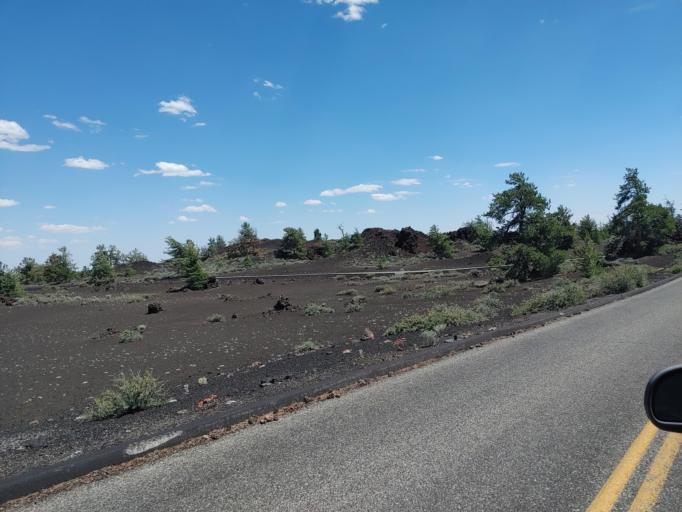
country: US
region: Idaho
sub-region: Butte County
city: Arco
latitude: 43.4524
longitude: -113.5436
